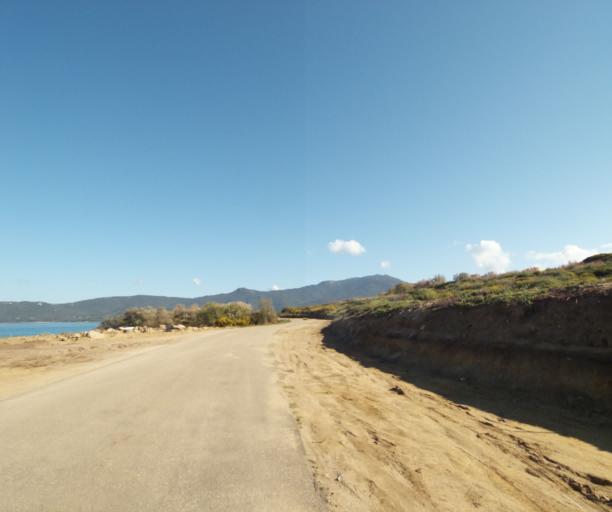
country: FR
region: Corsica
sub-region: Departement de la Corse-du-Sud
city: Propriano
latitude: 41.6644
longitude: 8.8824
